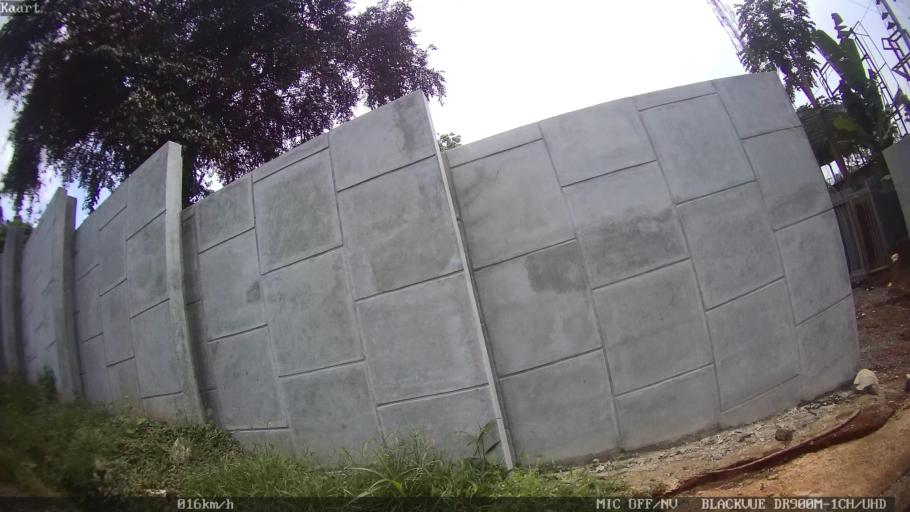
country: ID
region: Lampung
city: Bandarlampung
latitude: -5.4200
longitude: 105.2328
